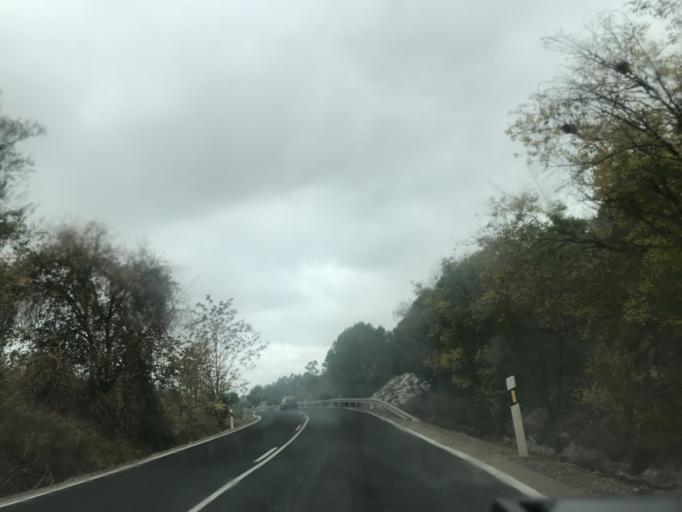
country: ES
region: Andalusia
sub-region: Provincia de Jaen
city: Peal de Becerro
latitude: 37.9171
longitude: -3.1079
